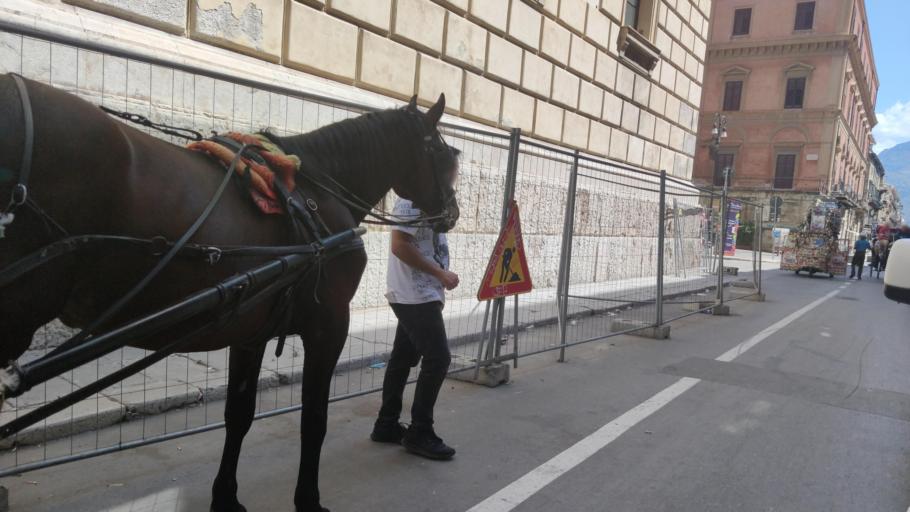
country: IT
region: Sicily
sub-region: Palermo
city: Palermo
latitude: 38.1150
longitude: 13.3619
